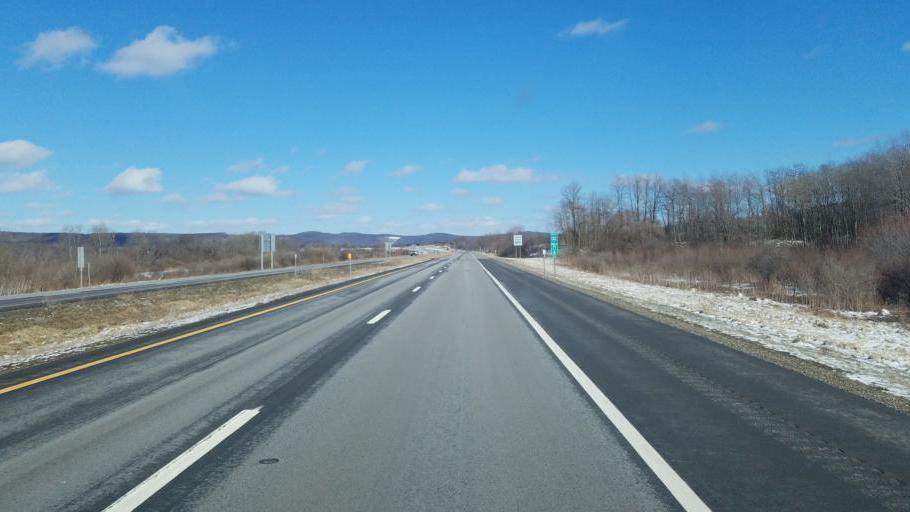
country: US
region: New York
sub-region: Cattaraugus County
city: Allegany
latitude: 42.0912
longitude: -78.5526
